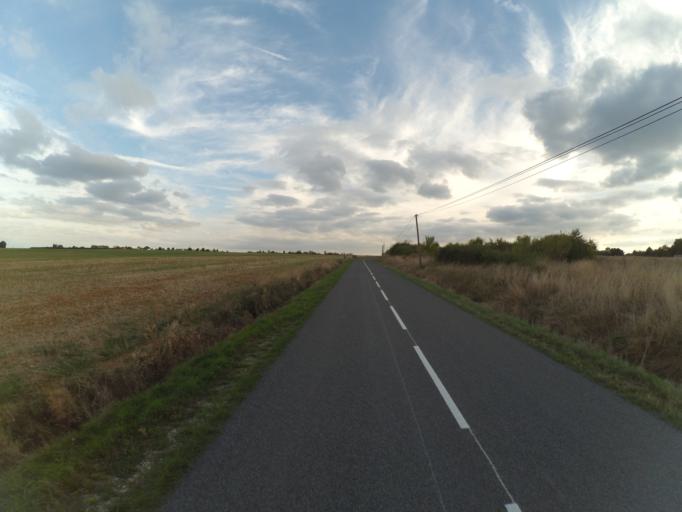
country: FR
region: Centre
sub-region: Departement d'Indre-et-Loire
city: Nazelles-Negron
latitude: 47.4491
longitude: 0.9501
